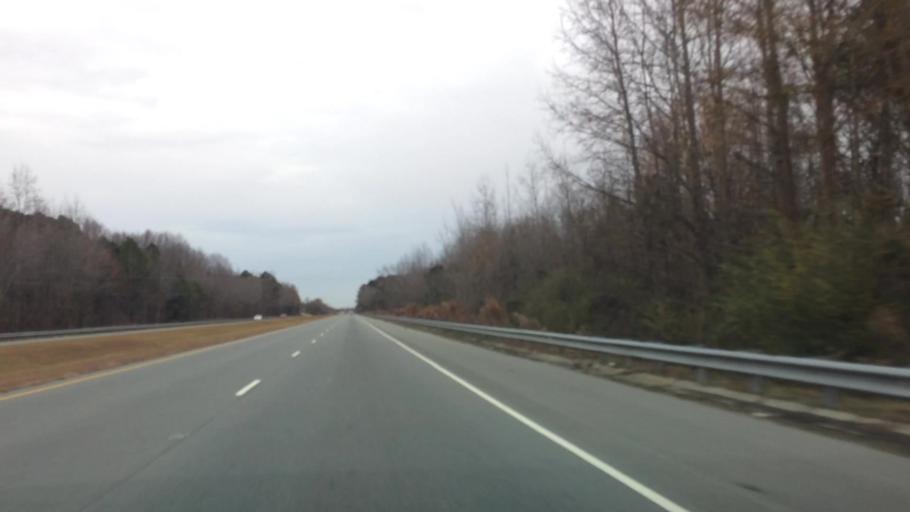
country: US
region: North Carolina
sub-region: Wayne County
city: Mount Olive
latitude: 35.1370
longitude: -78.1376
